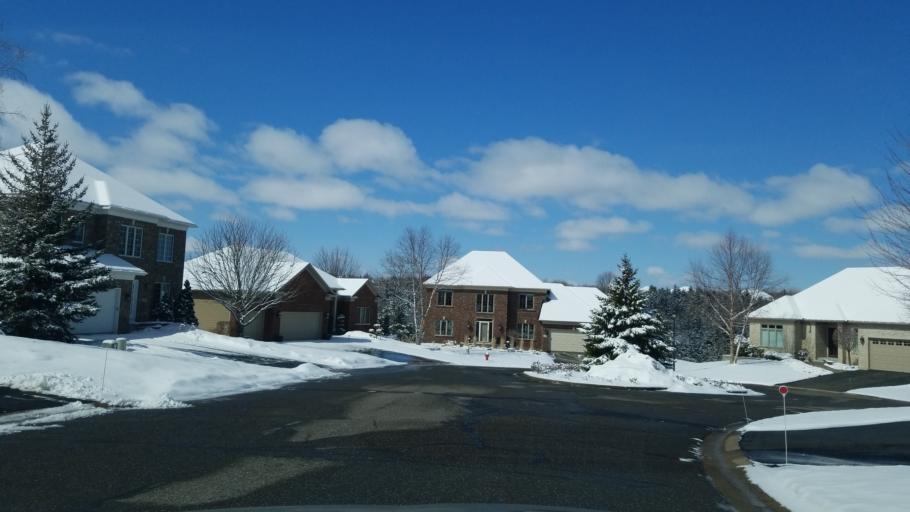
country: US
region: Wisconsin
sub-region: Saint Croix County
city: Hudson
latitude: 44.9558
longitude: -92.7025
